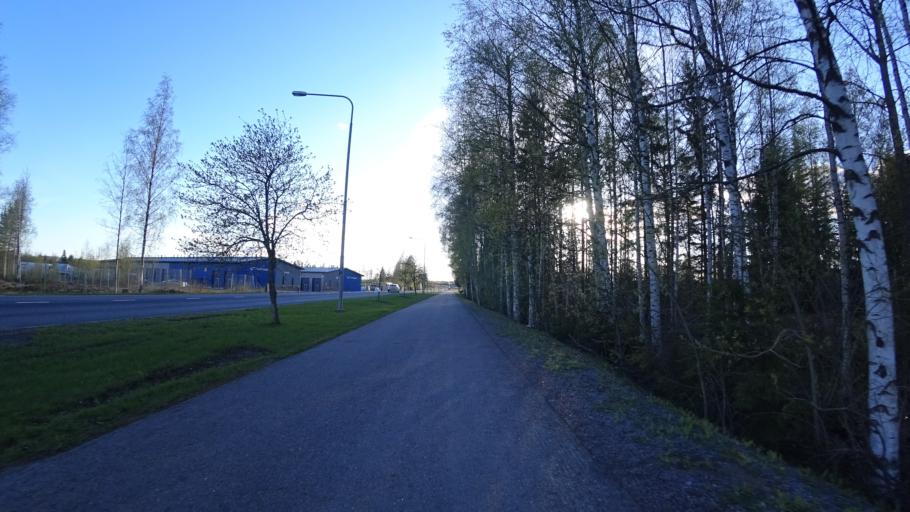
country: FI
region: Pirkanmaa
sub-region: Tampere
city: Yloejaervi
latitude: 61.5029
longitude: 23.5773
